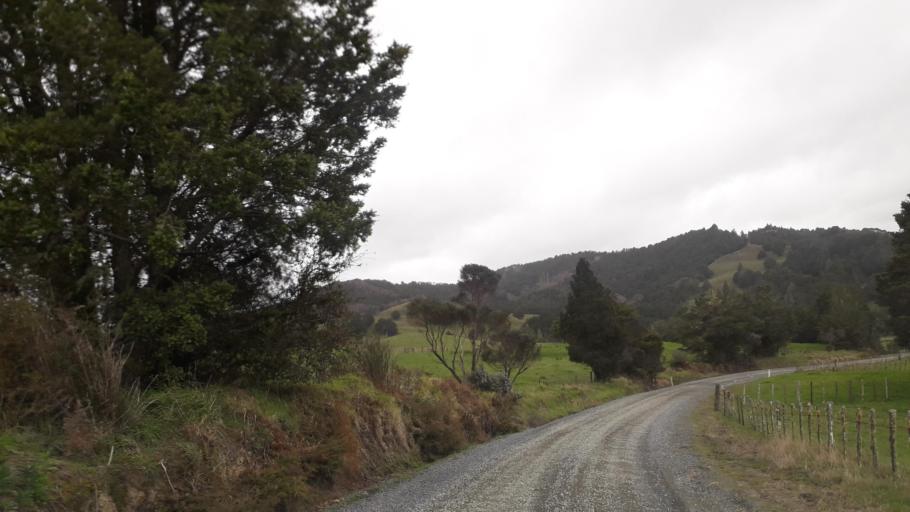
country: NZ
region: Northland
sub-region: Far North District
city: Waimate North
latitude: -35.1391
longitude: 173.7126
